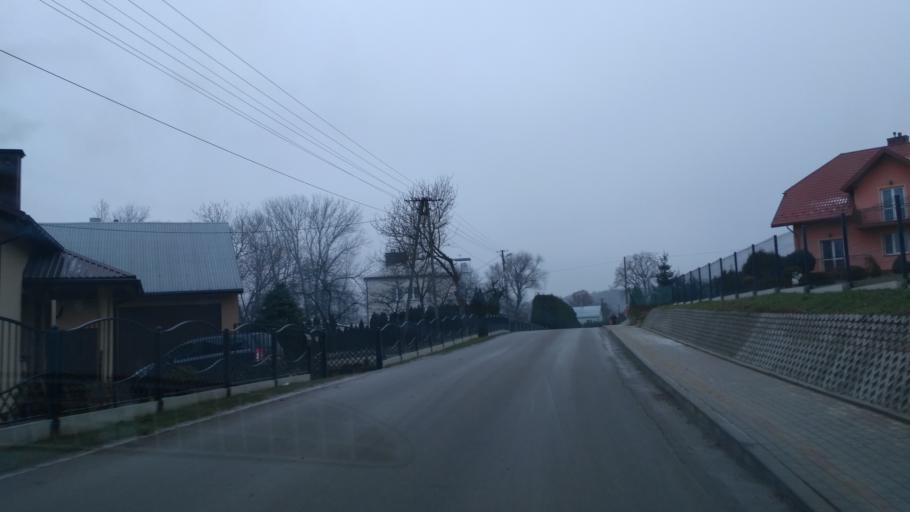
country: PL
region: Subcarpathian Voivodeship
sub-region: Powiat przeworski
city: Zarzecze
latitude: 49.9895
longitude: 22.5276
